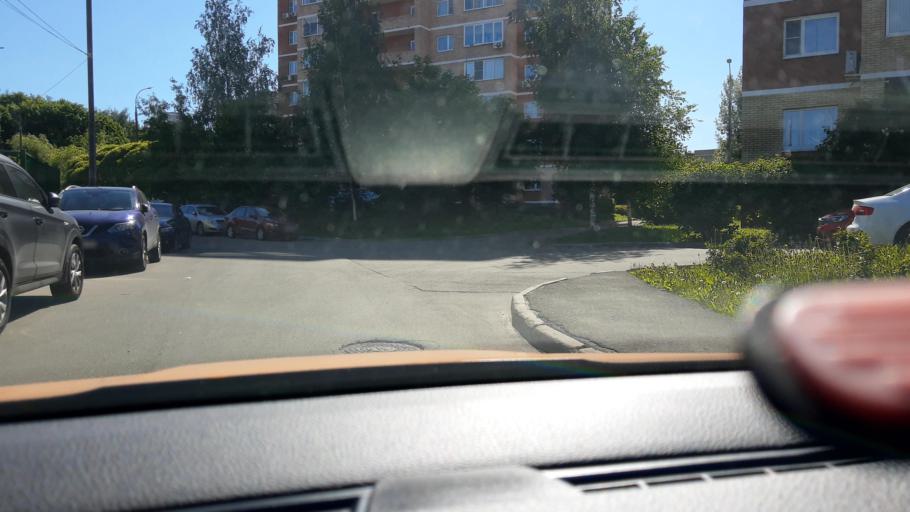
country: RU
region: Moscow
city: Khimki
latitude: 55.8904
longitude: 37.3940
